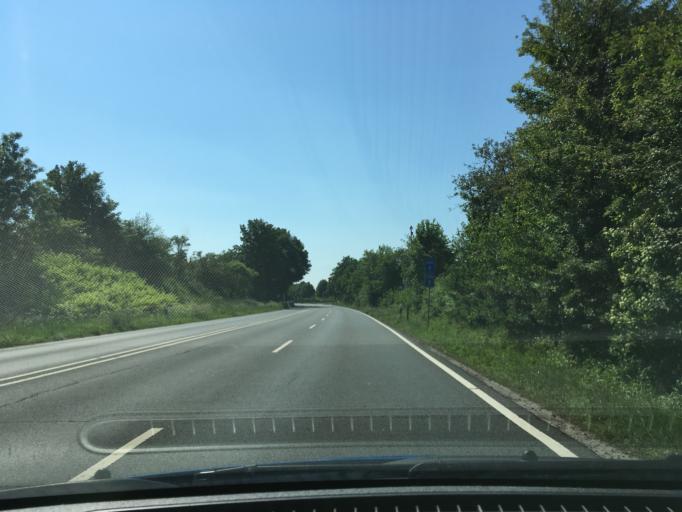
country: DE
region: North Rhine-Westphalia
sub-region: Regierungsbezirk Munster
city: Greven
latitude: 52.0965
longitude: 7.6305
